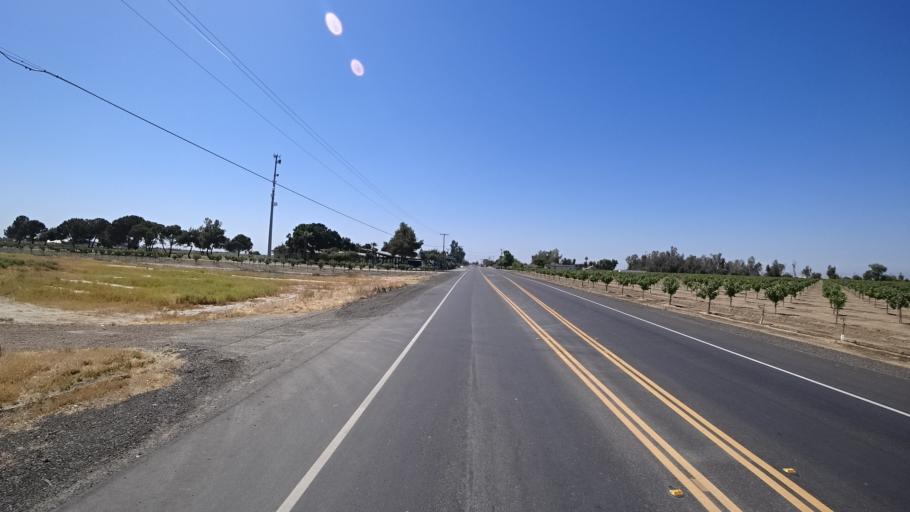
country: US
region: California
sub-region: Kings County
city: Lemoore
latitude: 36.2455
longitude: -119.7808
